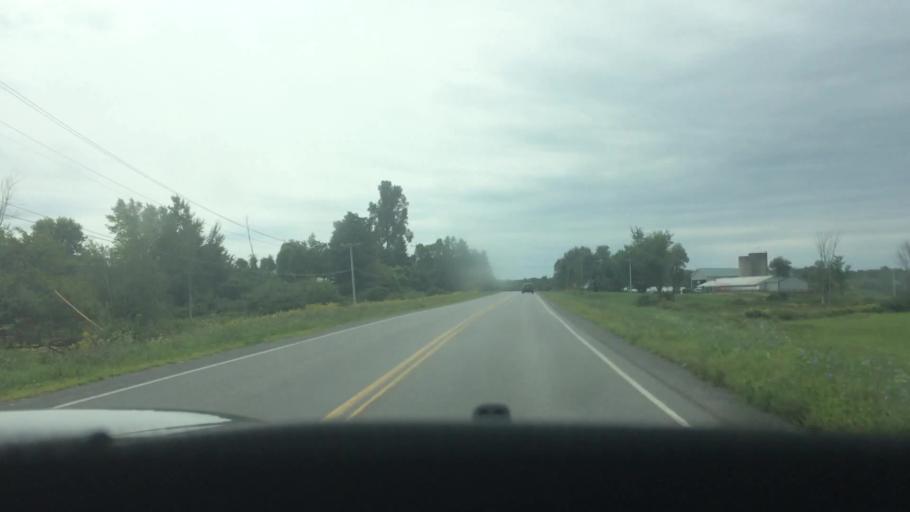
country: US
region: New York
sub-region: St. Lawrence County
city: Canton
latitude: 44.4904
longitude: -75.2491
